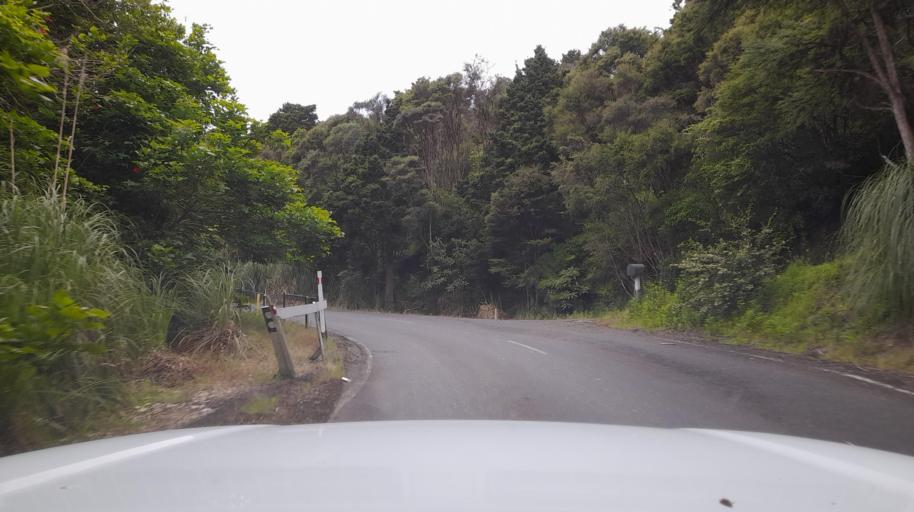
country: NZ
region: Northland
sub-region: Far North District
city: Kaitaia
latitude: -35.3605
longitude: 173.4588
